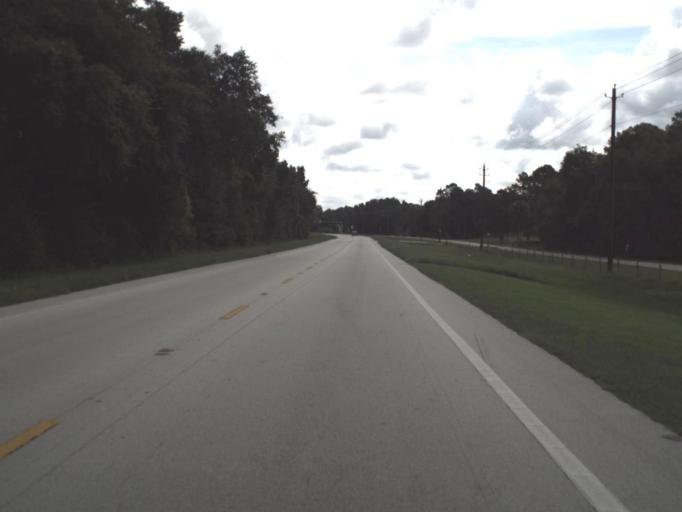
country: US
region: Florida
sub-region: Hillsborough County
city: Thonotosassa
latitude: 28.0941
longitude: -82.2599
